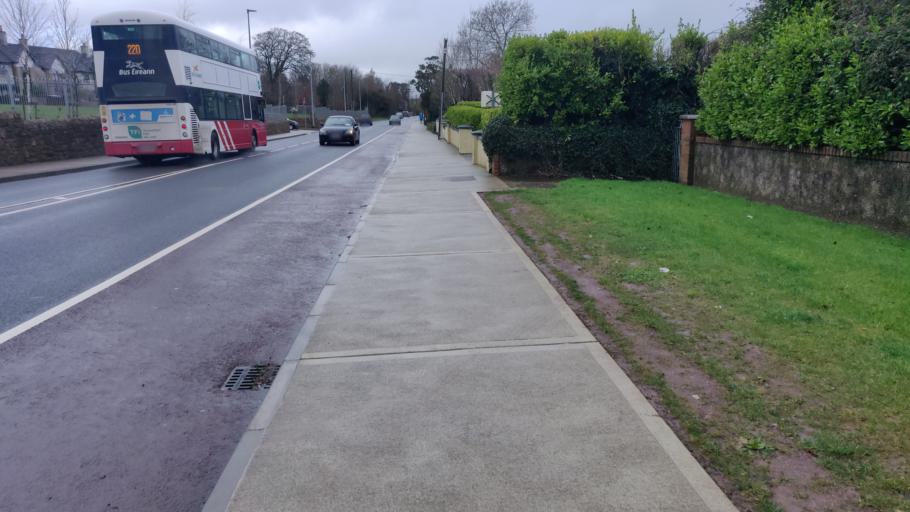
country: IE
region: Munster
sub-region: County Cork
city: Carrigaline
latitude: 51.8647
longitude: -8.4136
